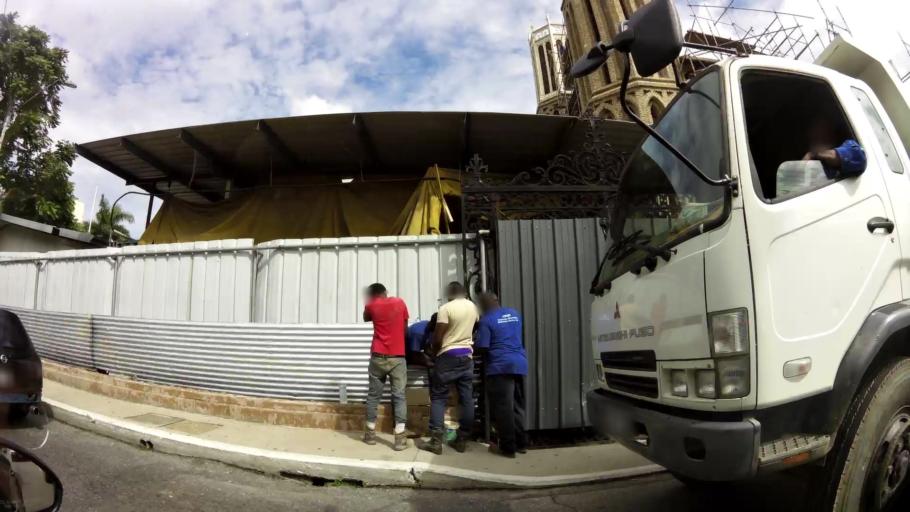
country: TT
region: San Juan/Laventille
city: Laventille
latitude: 10.6498
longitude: -61.5071
